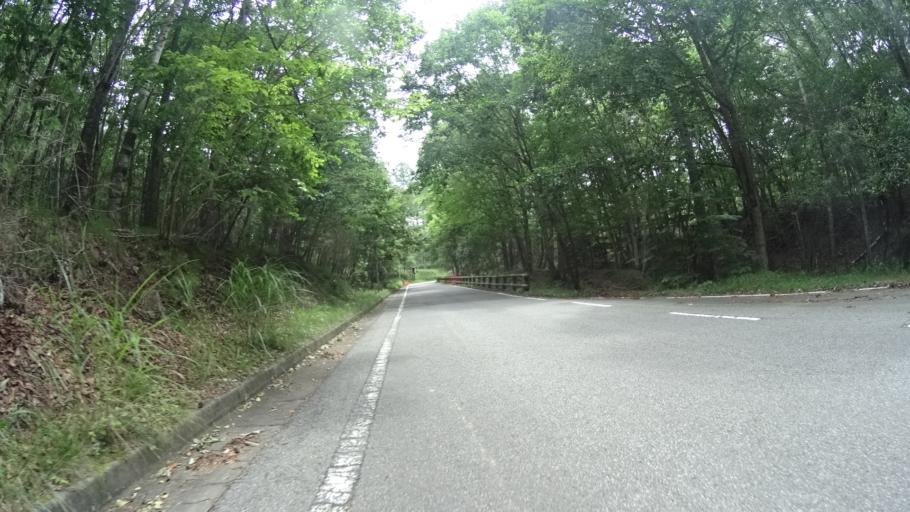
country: JP
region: Yamanashi
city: Nirasaki
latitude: 35.8883
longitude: 138.5697
